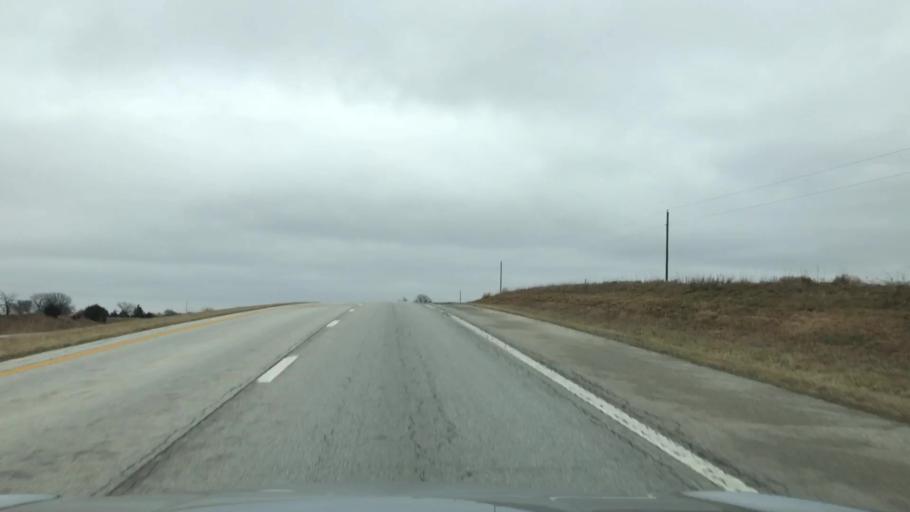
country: US
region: Missouri
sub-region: Linn County
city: Marceline
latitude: 39.7601
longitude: -92.9195
